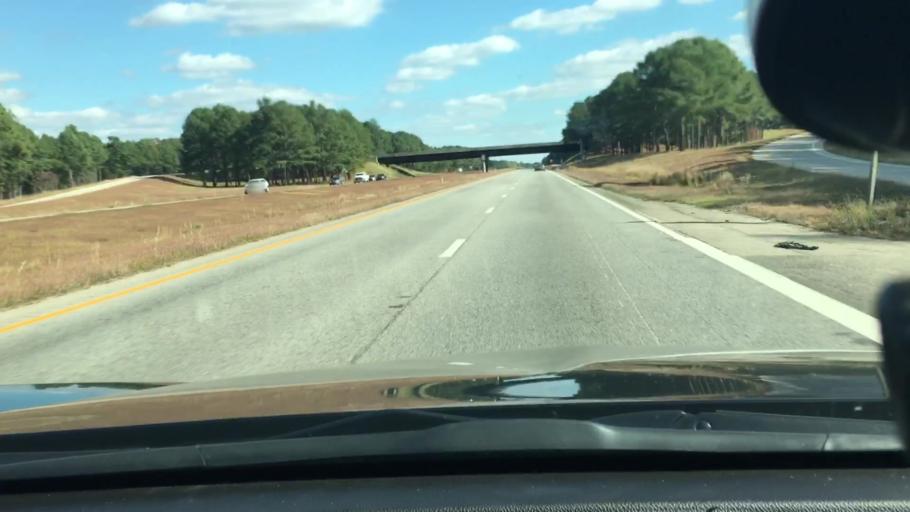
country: US
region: North Carolina
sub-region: Wilson County
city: Lucama
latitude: 35.7748
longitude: -78.0609
